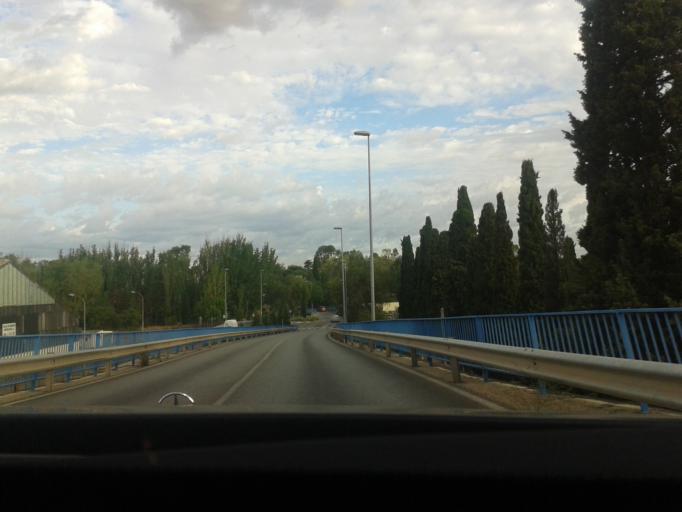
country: ES
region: Madrid
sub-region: Provincia de Madrid
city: Alcala de Henares
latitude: 40.4854
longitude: -3.3783
